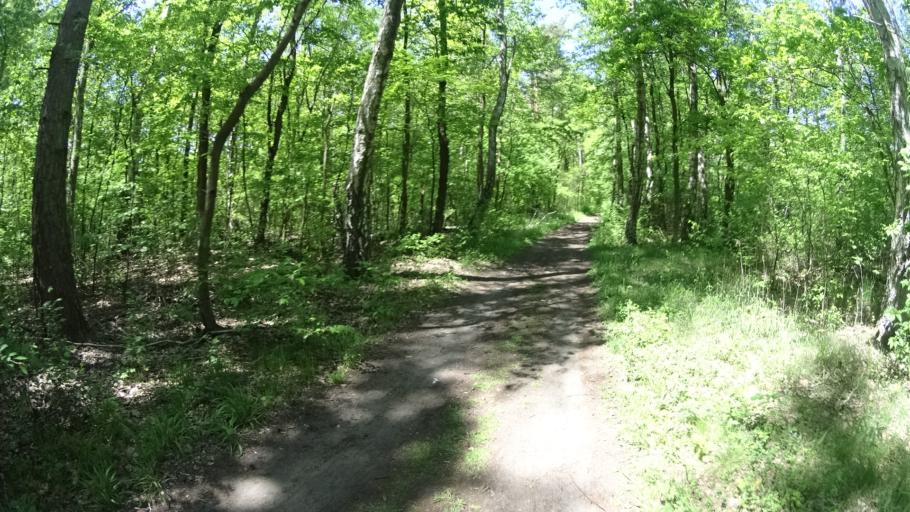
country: PL
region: Masovian Voivodeship
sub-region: Warszawa
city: Bemowo
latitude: 52.2704
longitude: 20.8855
